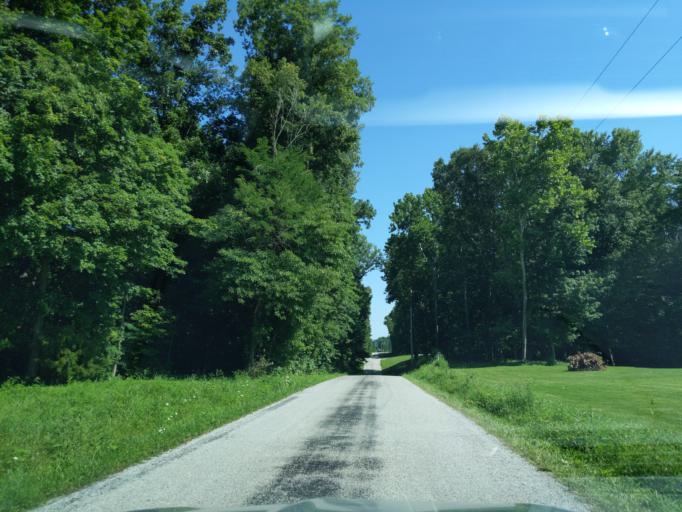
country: US
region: Indiana
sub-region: Ripley County
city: Osgood
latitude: 39.0963
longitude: -85.4324
